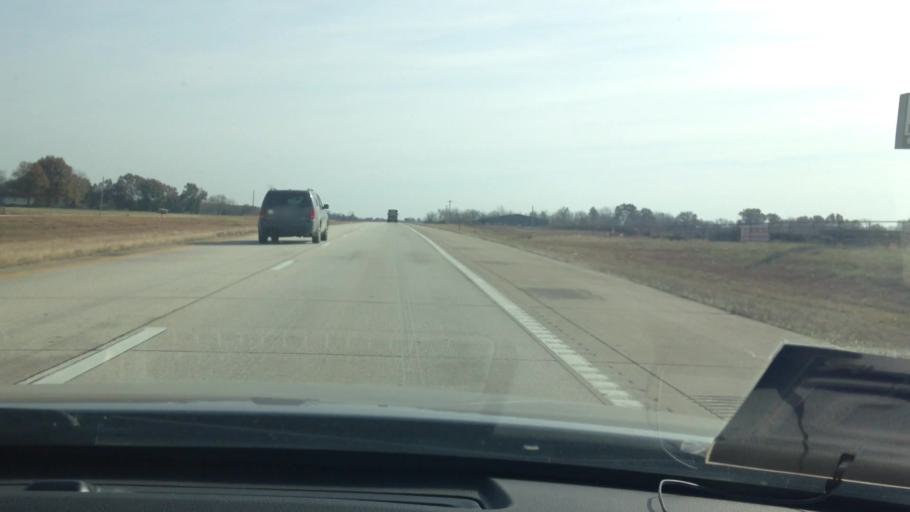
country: US
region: Missouri
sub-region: Henry County
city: Clinton
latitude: 38.4142
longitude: -93.8605
